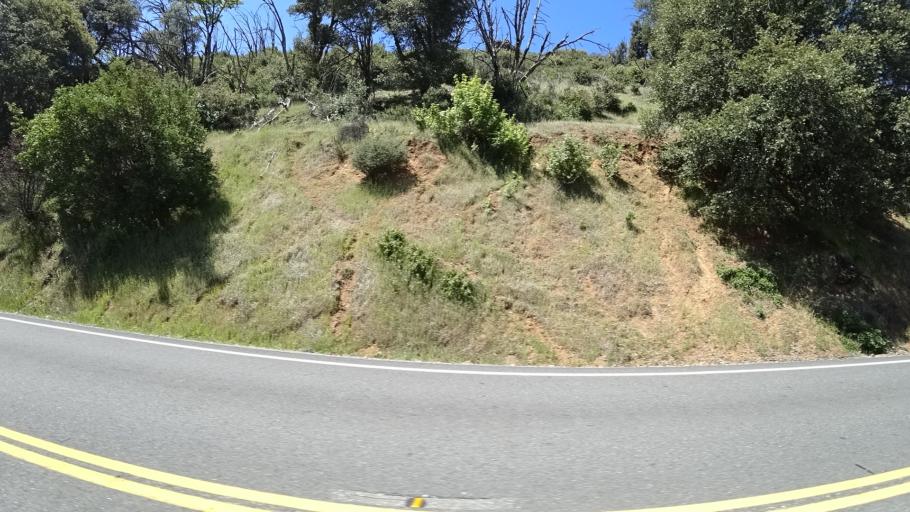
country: US
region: California
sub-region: Trinity County
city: Weaverville
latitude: 40.7368
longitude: -123.0082
